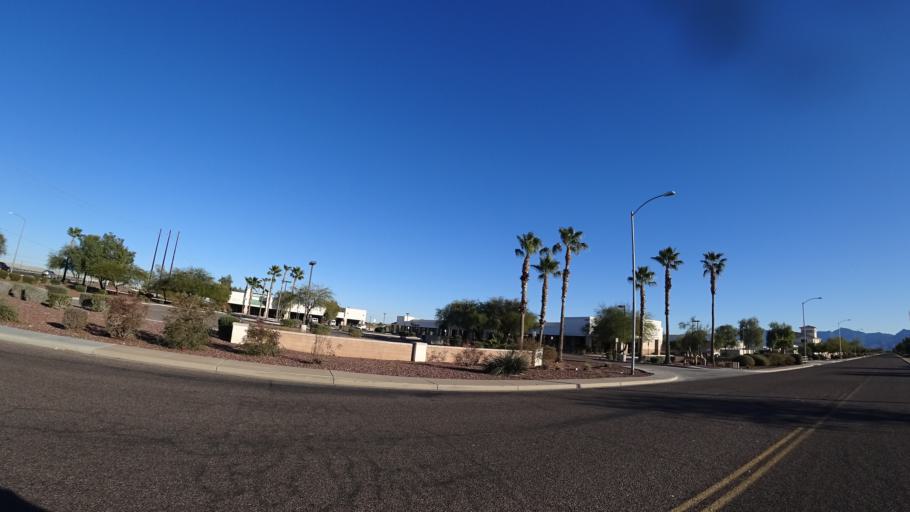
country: US
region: Arizona
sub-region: Maricopa County
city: Avondale
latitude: 33.4493
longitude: -112.3368
